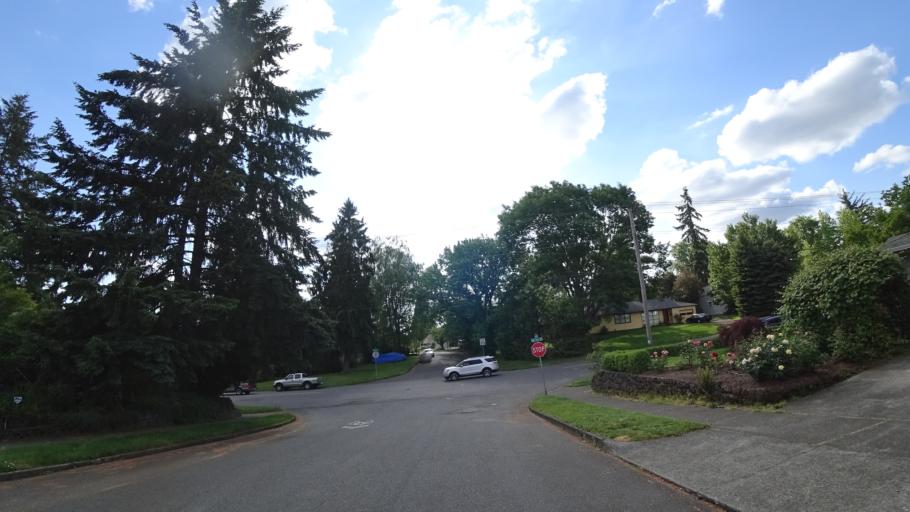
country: US
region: Oregon
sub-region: Washington County
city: Garden Home-Whitford
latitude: 45.4776
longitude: -122.7227
